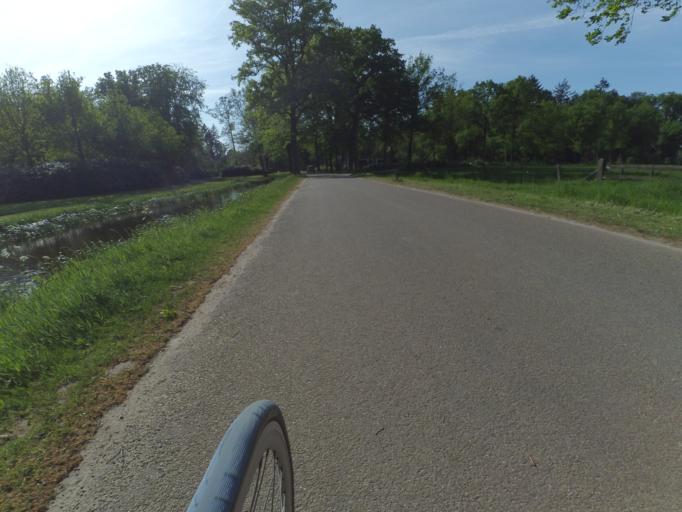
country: NL
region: Overijssel
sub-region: Gemeente Oldenzaal
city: Oldenzaal
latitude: 52.3760
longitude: 6.9822
